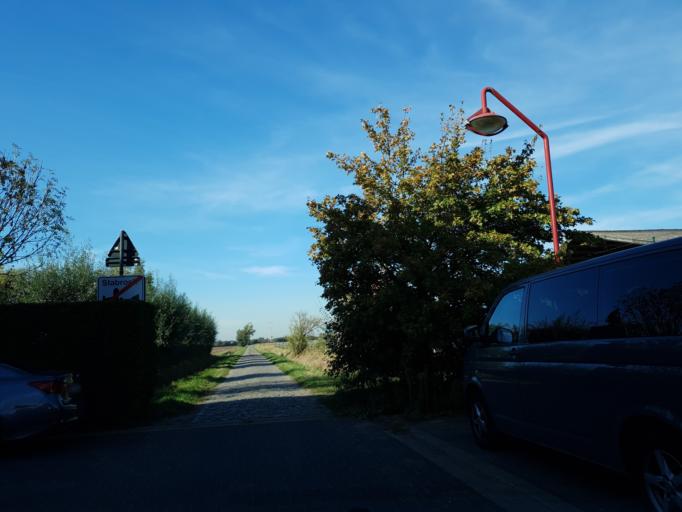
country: BE
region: Flanders
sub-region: Provincie Antwerpen
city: Stabroek
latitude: 51.3305
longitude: 4.3571
